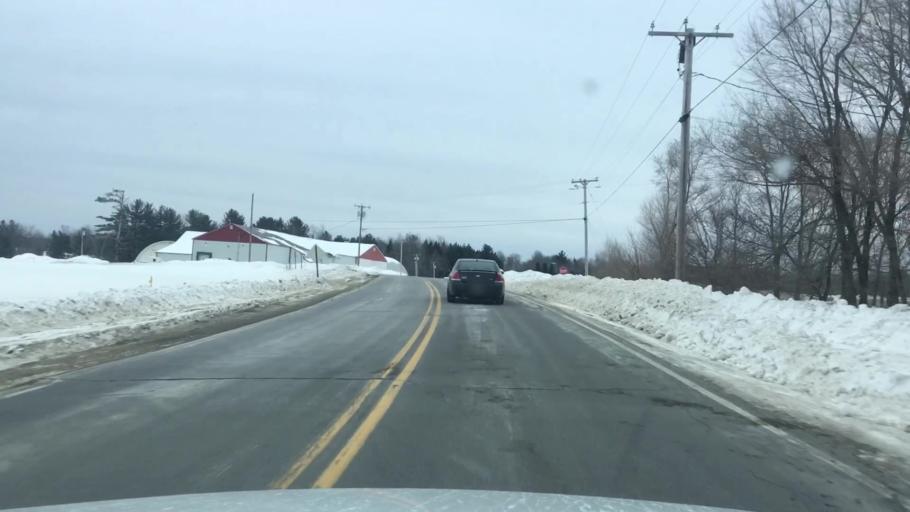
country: US
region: Maine
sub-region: Penobscot County
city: Garland
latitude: 44.9896
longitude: -69.0877
